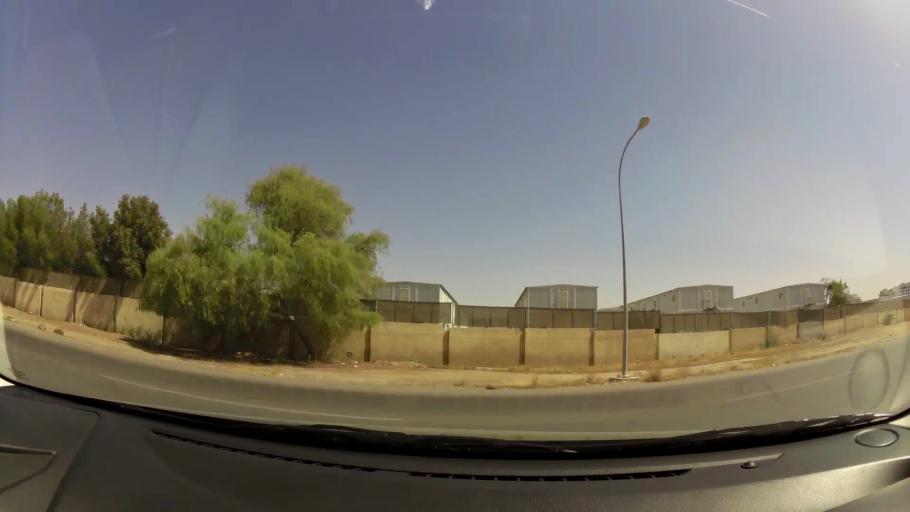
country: OM
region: Muhafazat Masqat
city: Bawshar
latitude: 23.5971
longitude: 58.3545
